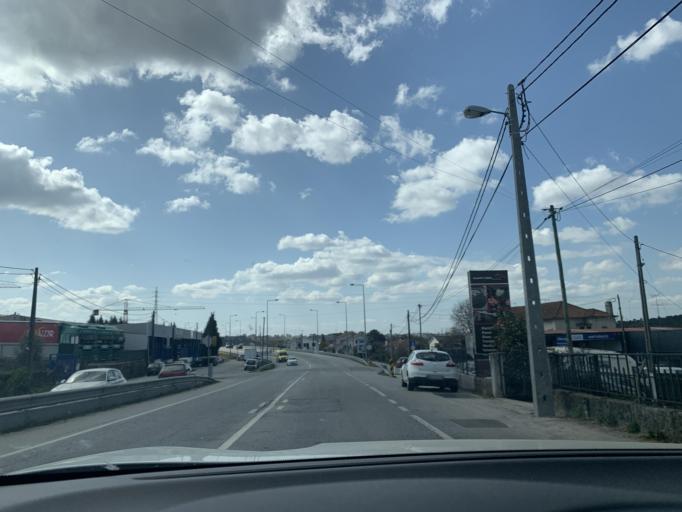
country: PT
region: Viseu
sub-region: Viseu
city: Rio de Loba
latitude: 40.6835
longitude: -7.8819
